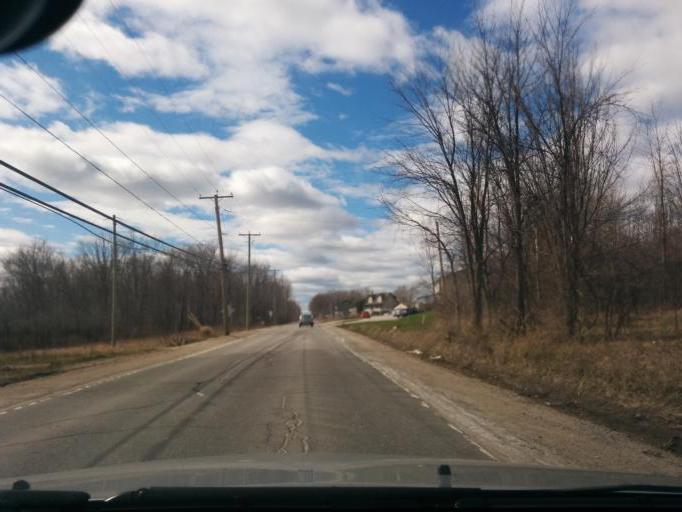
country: CA
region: Ontario
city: Bells Corners
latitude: 45.4369
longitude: -75.9105
